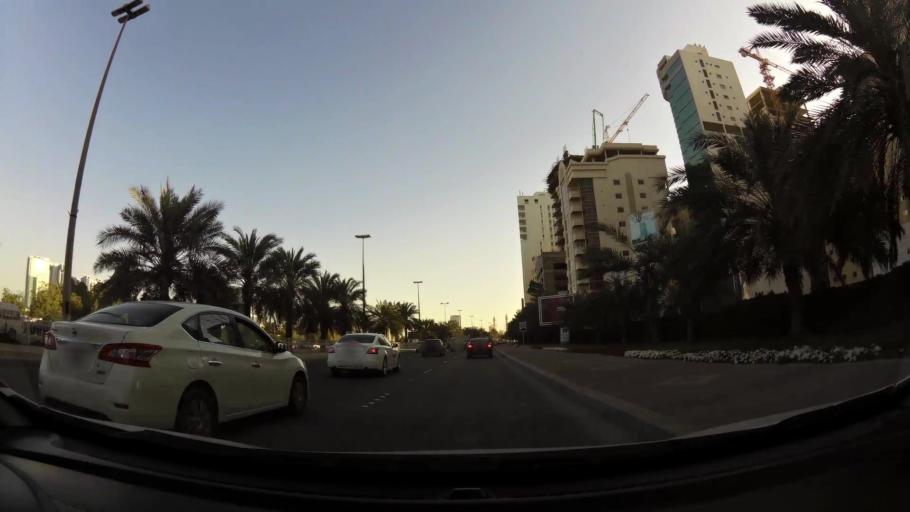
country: BH
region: Manama
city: Manama
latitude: 26.2294
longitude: 50.5987
